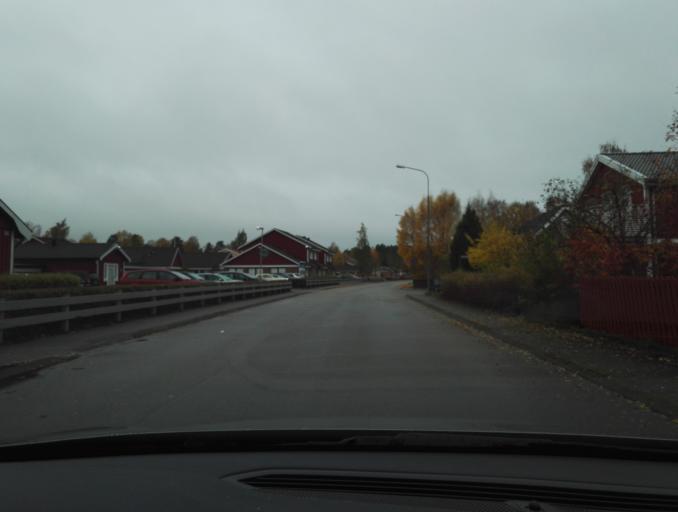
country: SE
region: Kronoberg
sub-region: Vaxjo Kommun
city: Rottne
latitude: 57.0246
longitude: 14.8967
